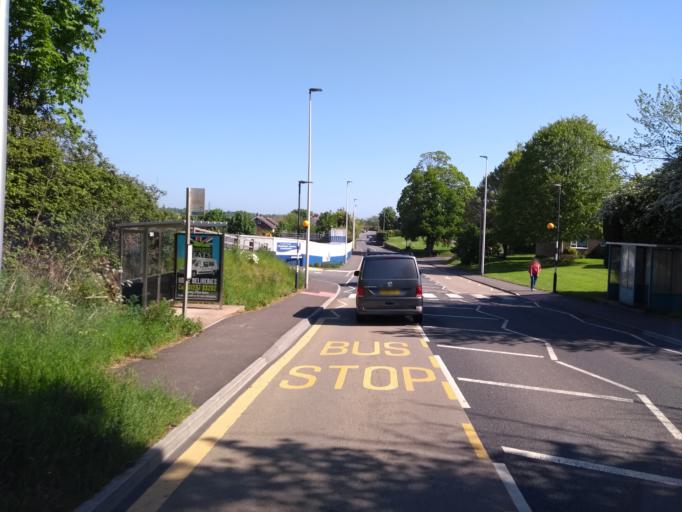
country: GB
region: England
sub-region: Devon
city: Axminster
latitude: 50.7882
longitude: -2.9886
